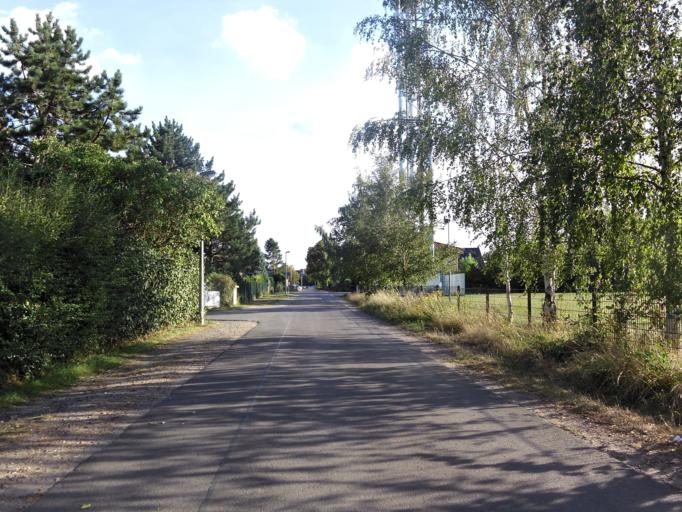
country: DE
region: Saxony
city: Markranstadt
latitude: 51.3475
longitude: 12.2699
